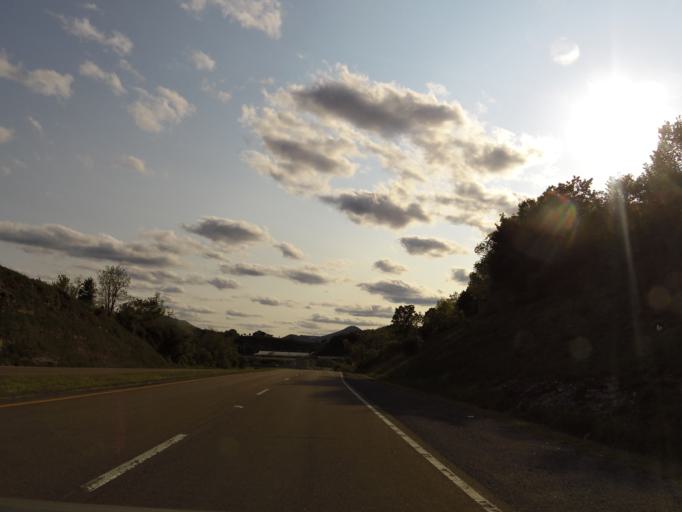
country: US
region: Virginia
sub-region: Tazewell County
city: Tazewell
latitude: 37.1300
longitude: -81.5207
